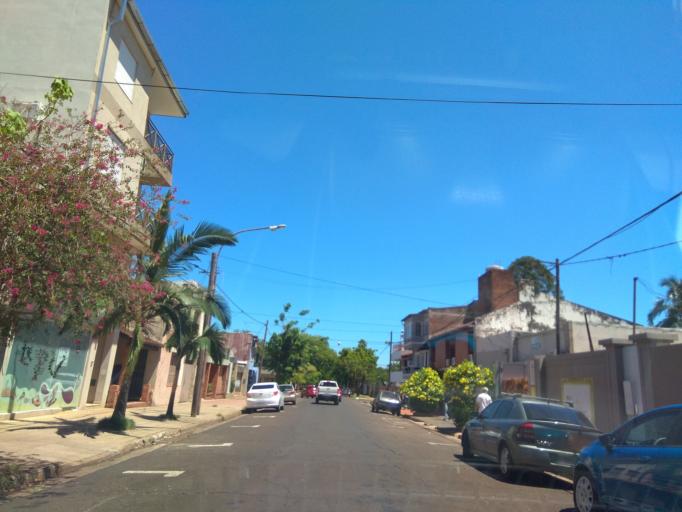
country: AR
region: Misiones
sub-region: Departamento de Capital
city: Posadas
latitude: -27.3627
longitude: -55.8986
